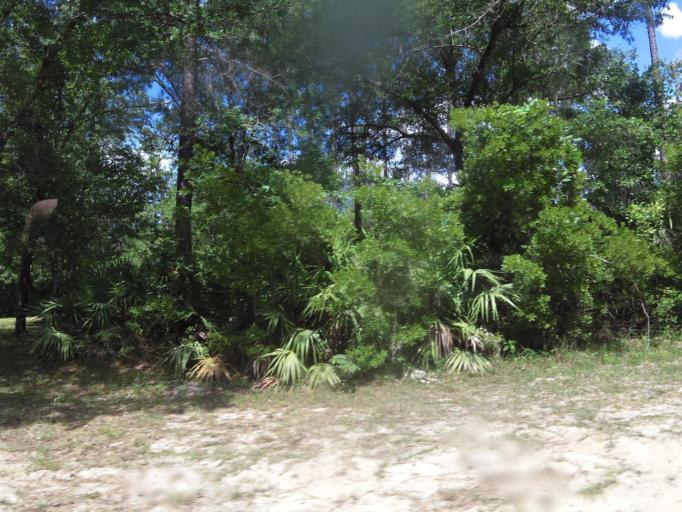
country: US
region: Florida
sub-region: Clay County
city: Asbury Lake
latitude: 29.8944
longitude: -81.8758
